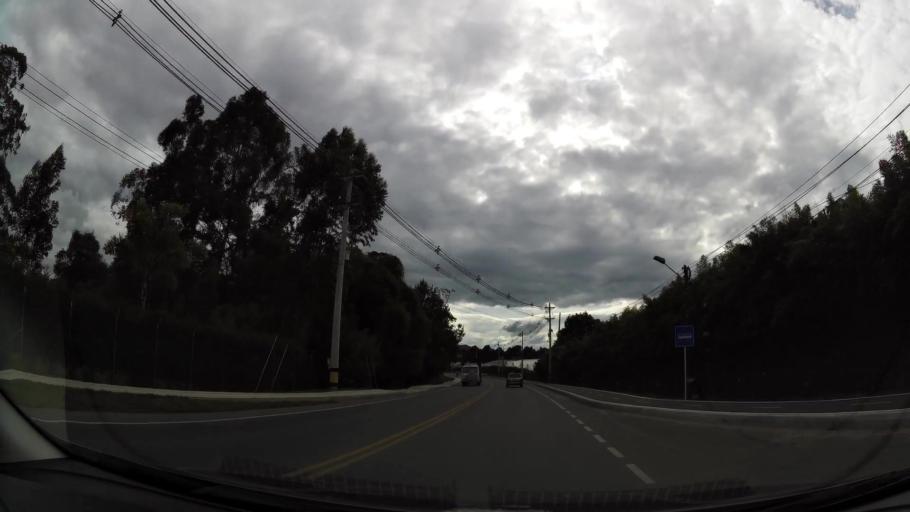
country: CO
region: Antioquia
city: Rionegro
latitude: 6.1450
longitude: -75.4298
